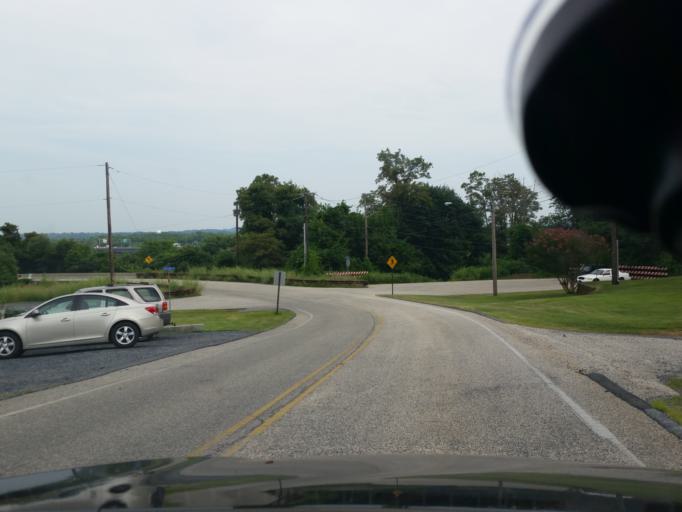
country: US
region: Pennsylvania
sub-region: Perry County
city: Marysville
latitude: 40.3183
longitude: -76.9172
